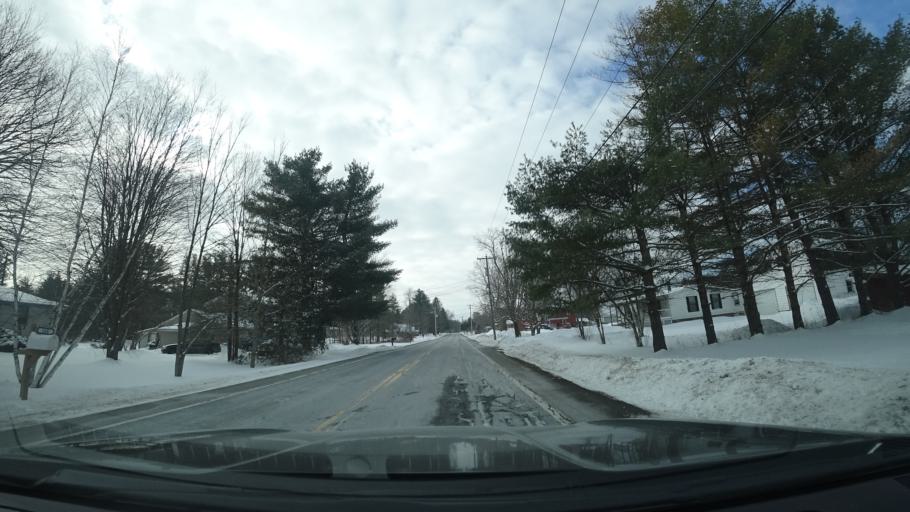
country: US
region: New York
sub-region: Washington County
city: Fort Edward
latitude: 43.2744
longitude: -73.6088
